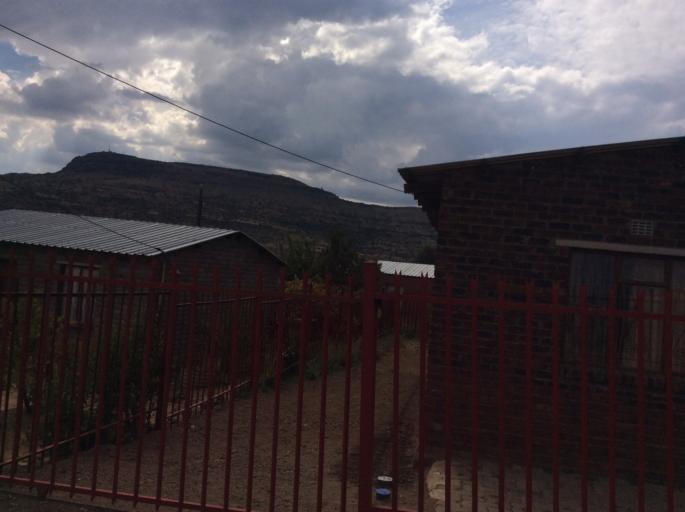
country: LS
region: Mafeteng
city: Mafeteng
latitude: -29.7226
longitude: 27.0296
